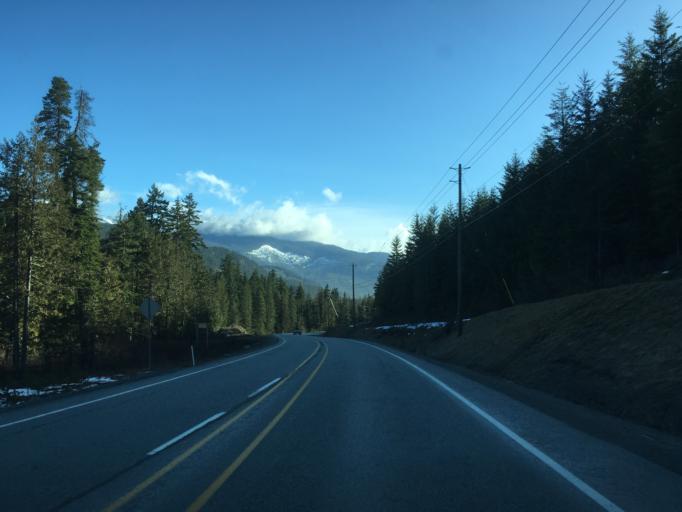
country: CA
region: British Columbia
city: Whistler
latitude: 50.0679
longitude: -123.1088
